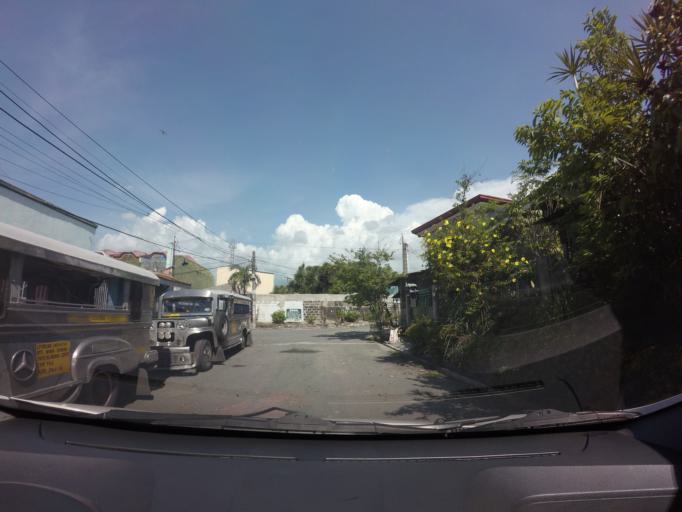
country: PH
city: Sambayanihan People's Village
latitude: 14.4423
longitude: 120.9951
